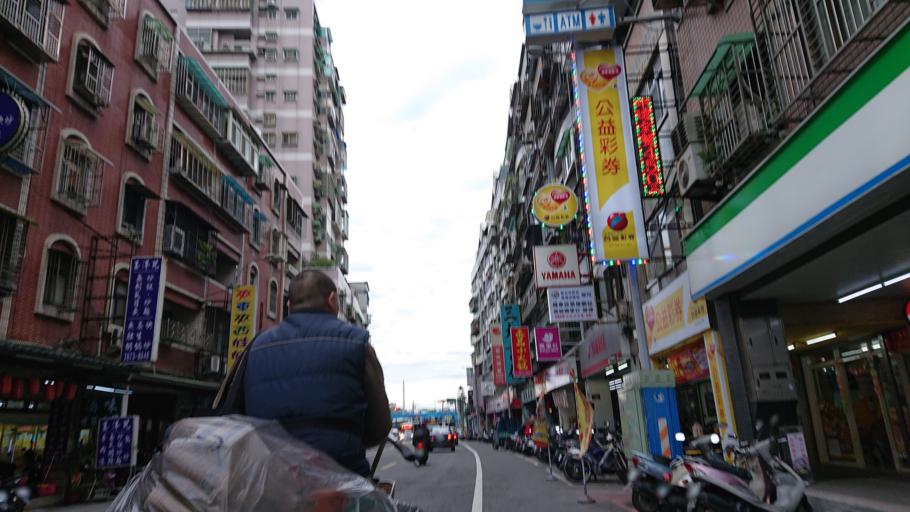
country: TW
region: Taiwan
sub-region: Taoyuan
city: Taoyuan
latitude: 24.9290
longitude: 121.3776
